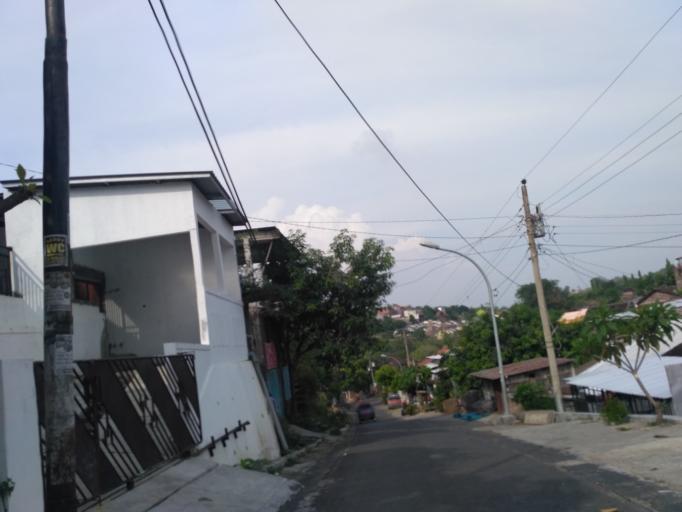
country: ID
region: Central Java
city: Semarang
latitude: -7.0190
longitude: 110.4475
